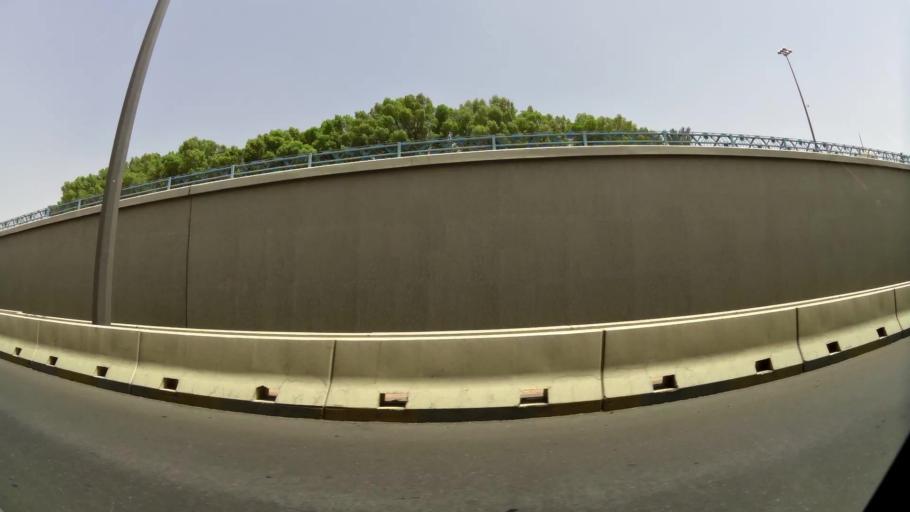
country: AE
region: Abu Dhabi
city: Al Ain
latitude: 24.2054
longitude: 55.7603
